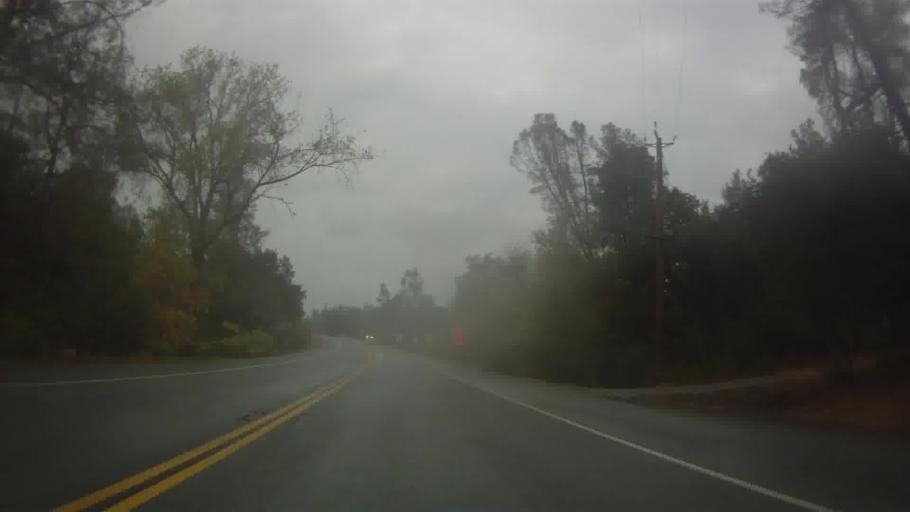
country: US
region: California
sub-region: Shasta County
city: Shasta
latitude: 40.5951
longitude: -122.4866
